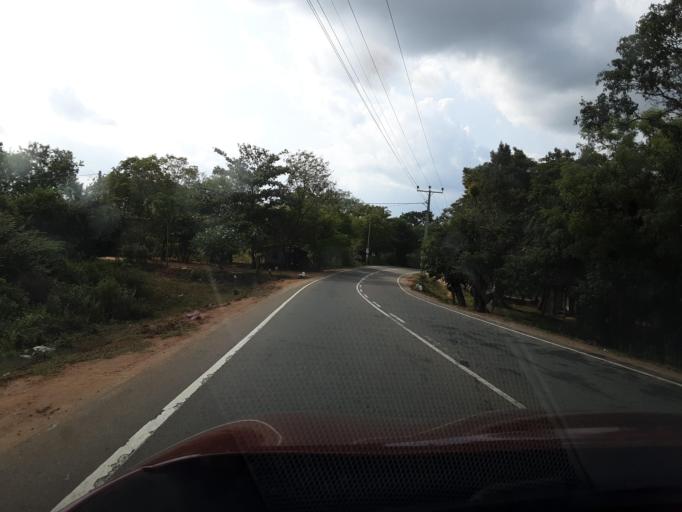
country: LK
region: Uva
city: Haputale
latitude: 6.5093
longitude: 81.1299
